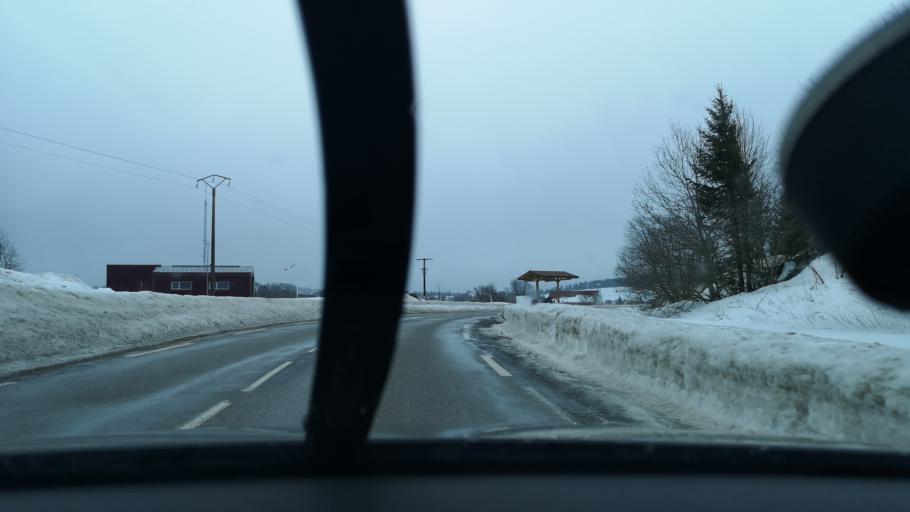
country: FR
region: Franche-Comte
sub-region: Departement du Doubs
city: Les Fourgs
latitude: 46.8421
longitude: 6.3935
